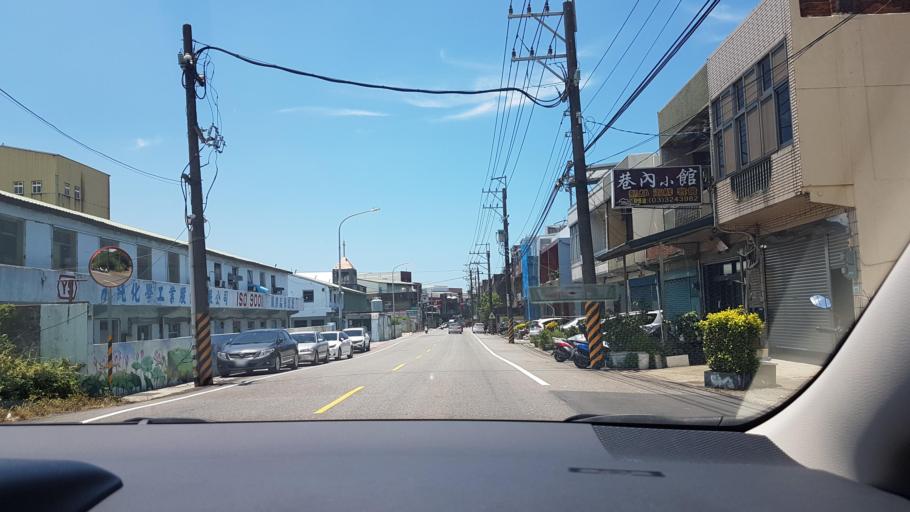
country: TW
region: Taiwan
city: Taoyuan City
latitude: 25.0919
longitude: 121.2706
